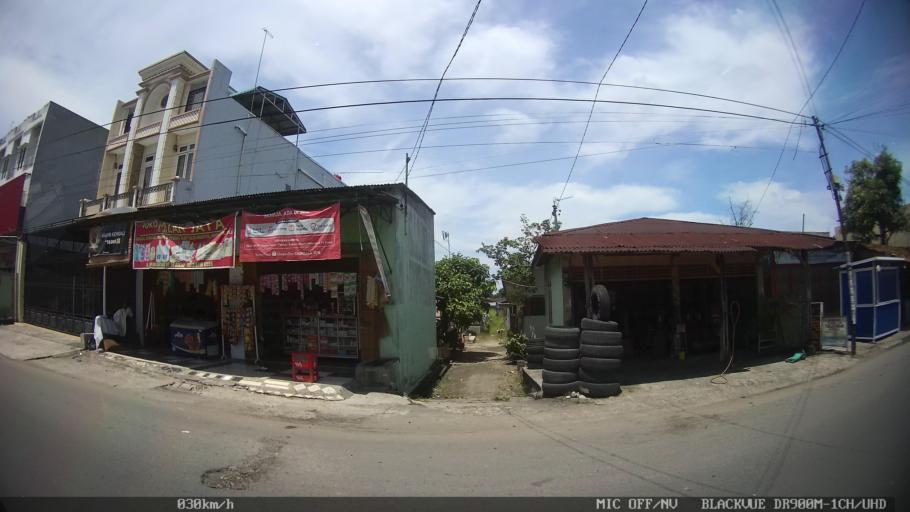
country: ID
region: North Sumatra
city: Binjai
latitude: 3.5967
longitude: 98.4902
